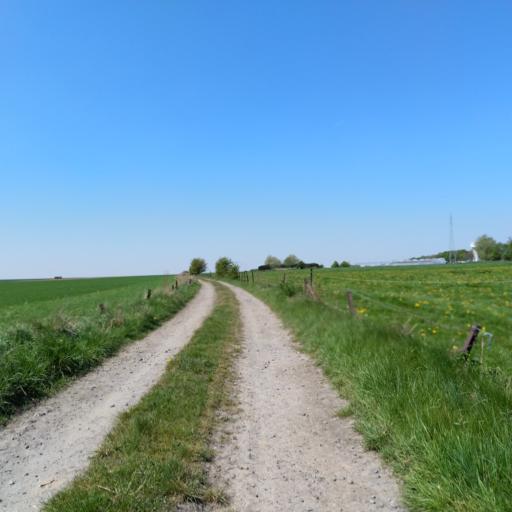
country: BE
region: Wallonia
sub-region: Province du Hainaut
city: Lens
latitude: 50.5601
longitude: 3.8926
